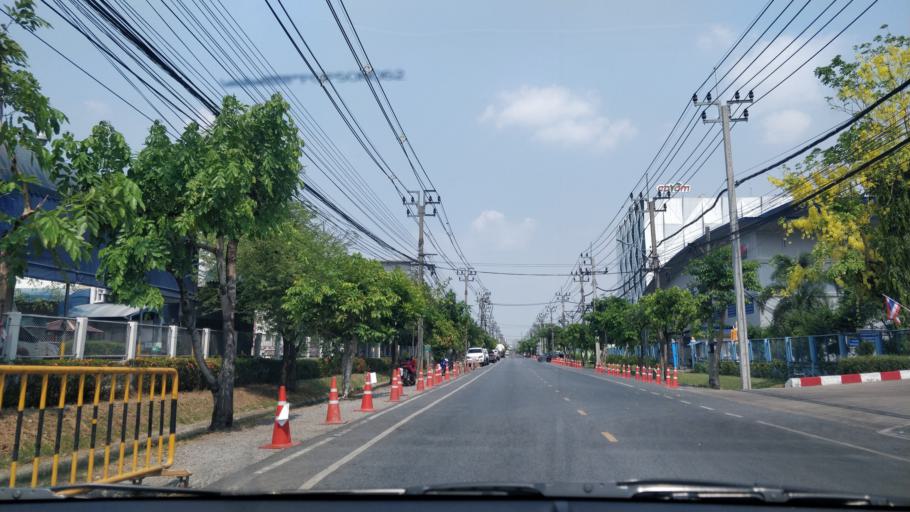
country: TH
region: Bangkok
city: Lat Krabang
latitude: 13.7713
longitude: 100.7844
